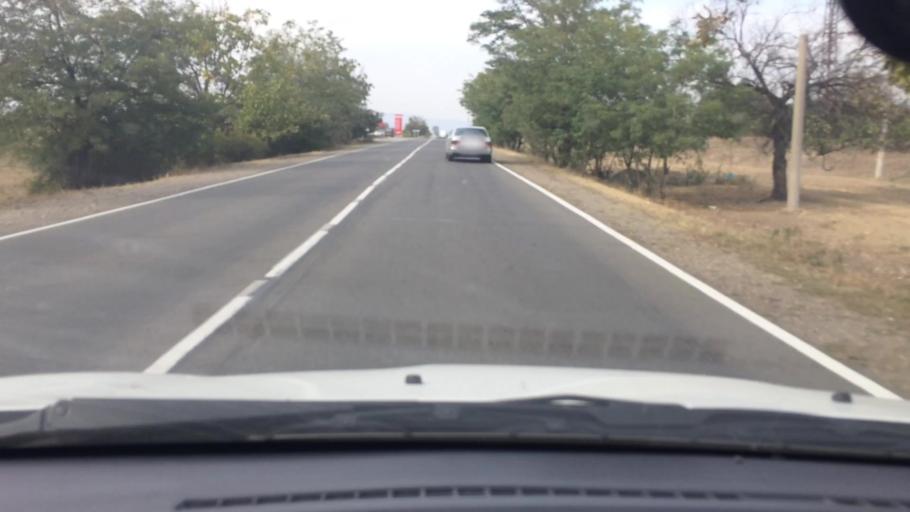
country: GE
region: Kvemo Kartli
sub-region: Marneuli
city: Marneuli
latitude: 41.4282
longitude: 44.8221
